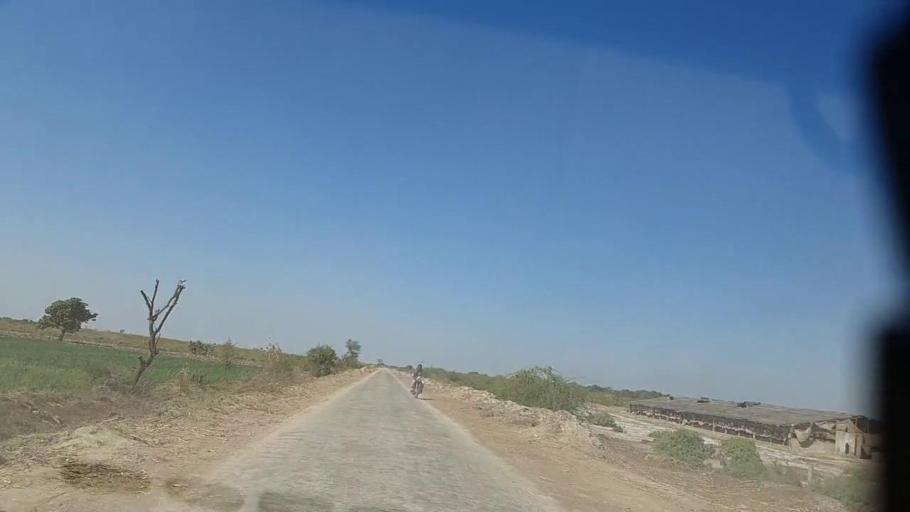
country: PK
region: Sindh
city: Mirwah Gorchani
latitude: 25.2215
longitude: 69.0245
